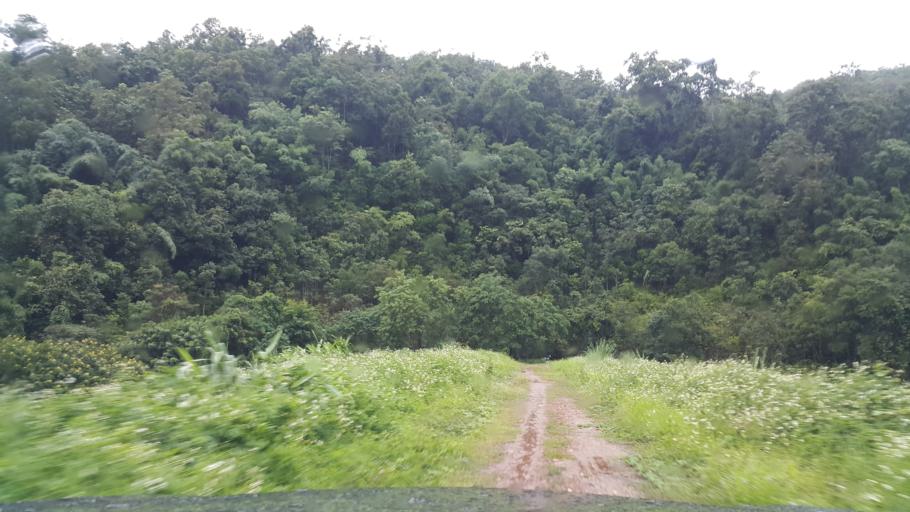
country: TH
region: Phayao
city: Phu Sang
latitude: 19.6253
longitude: 100.4160
